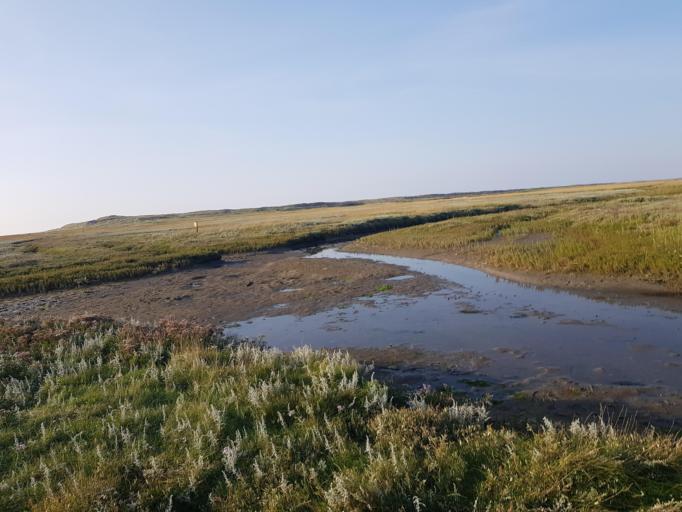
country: NL
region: North Holland
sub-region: Gemeente Texel
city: Den Burg
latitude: 53.1347
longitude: 4.8113
